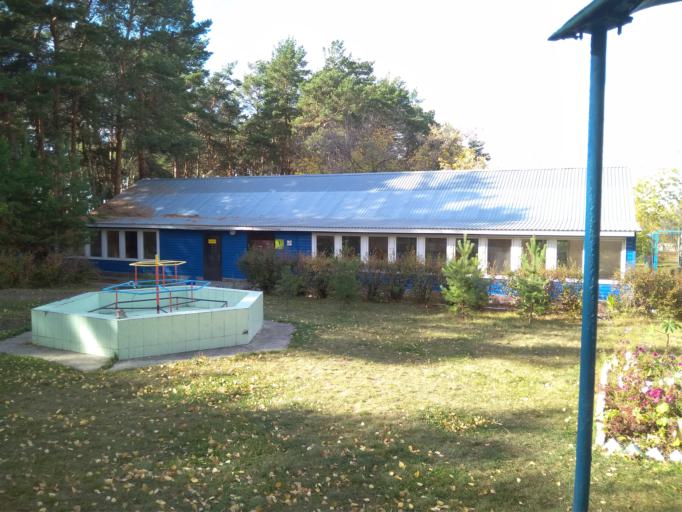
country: RU
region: Chelyabinsk
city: Troitsk
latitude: 54.0532
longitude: 61.6218
